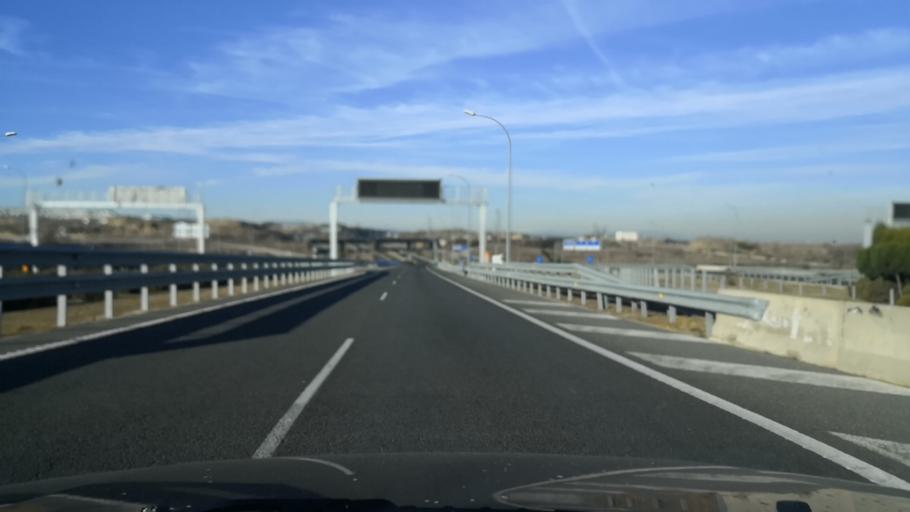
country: ES
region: Madrid
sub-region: Provincia de Madrid
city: Barajas de Madrid
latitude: 40.4988
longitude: -3.6018
